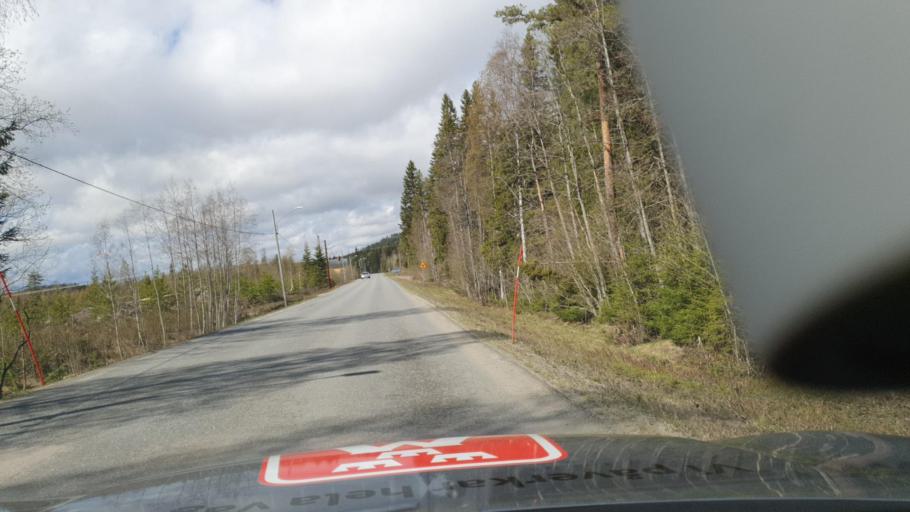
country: SE
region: Vaesternorrland
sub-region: OErnskoeldsviks Kommun
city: Ornskoldsvik
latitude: 63.6926
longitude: 18.8471
